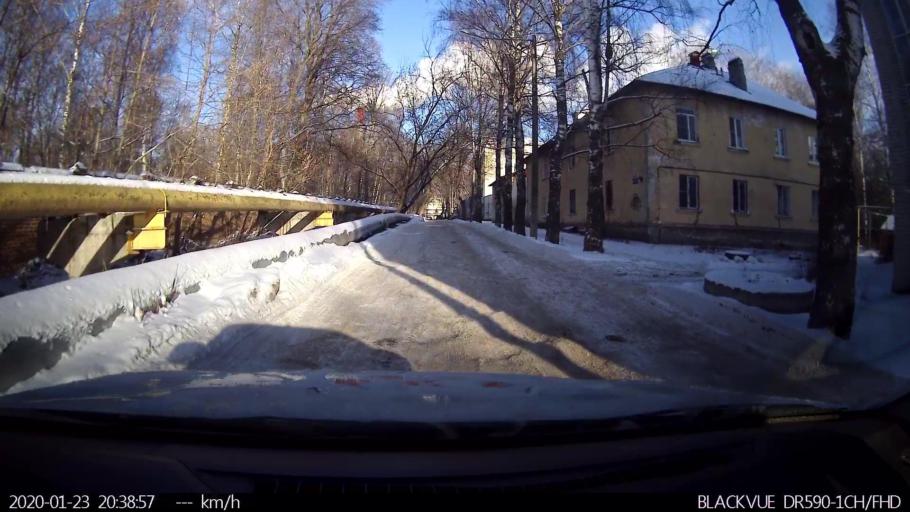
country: RU
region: Nizjnij Novgorod
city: Nizhniy Novgorod
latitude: 56.2989
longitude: 43.9972
